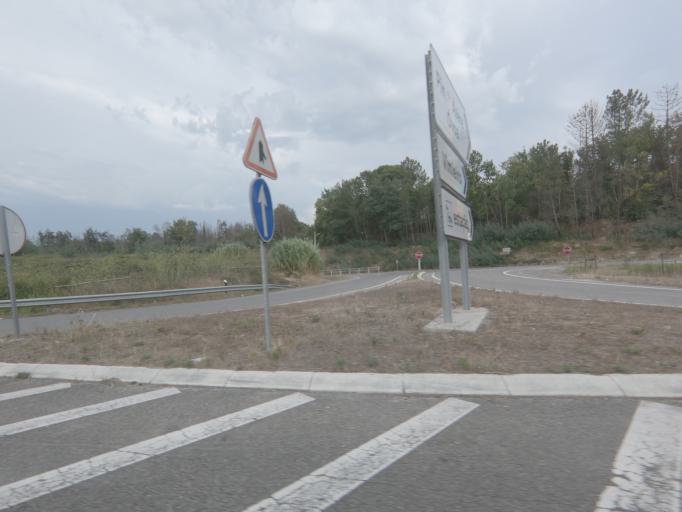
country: PT
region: Viseu
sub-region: Santa Comba Dao
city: Santa Comba Dao
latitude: 40.3911
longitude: -8.1281
